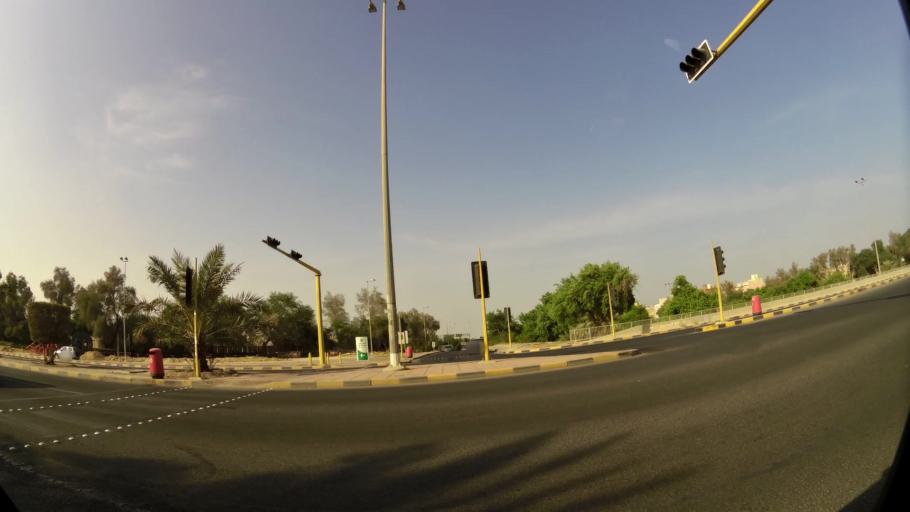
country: KW
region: Mubarak al Kabir
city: Mubarak al Kabir
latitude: 29.1747
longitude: 48.0914
